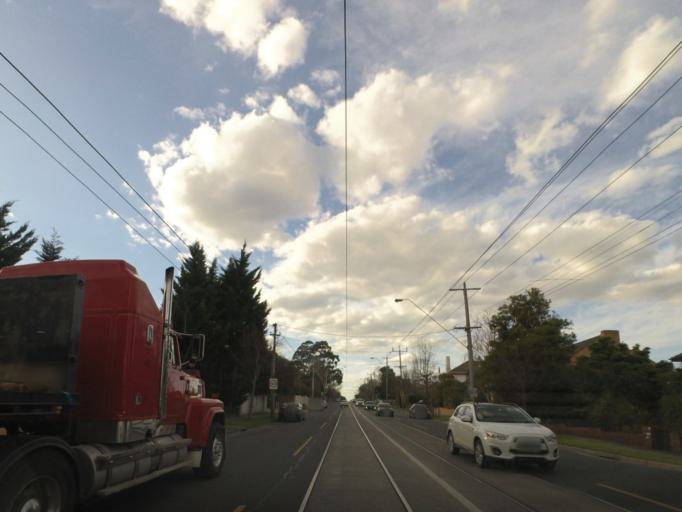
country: AU
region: Victoria
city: Glenferrie
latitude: -37.8412
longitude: 145.0547
